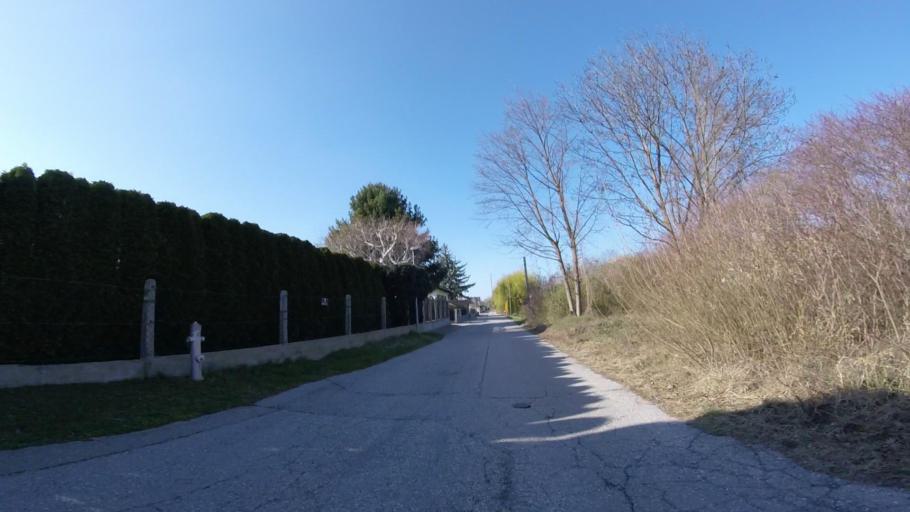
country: AT
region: Lower Austria
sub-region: Politischer Bezirk Baden
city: Ebreichsdorf
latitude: 47.9692
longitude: 16.4050
